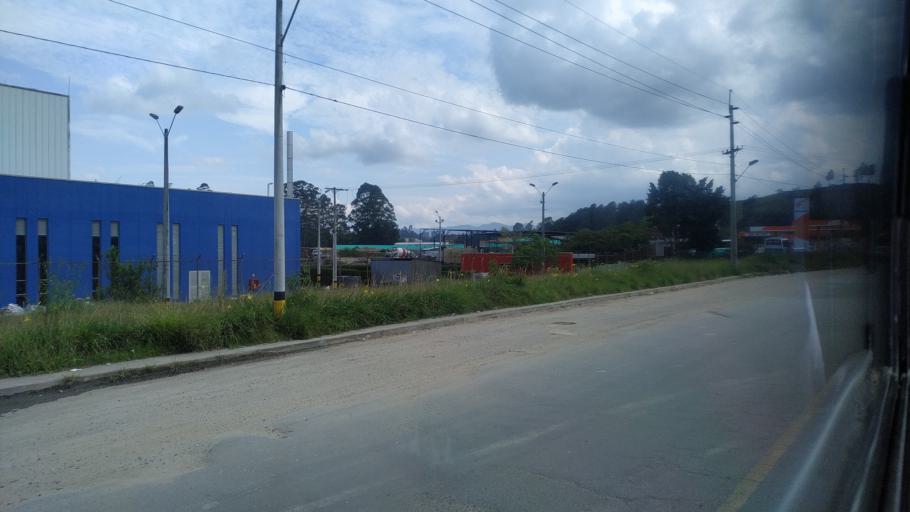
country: CO
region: Antioquia
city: Rionegro
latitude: 6.1748
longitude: -75.3693
